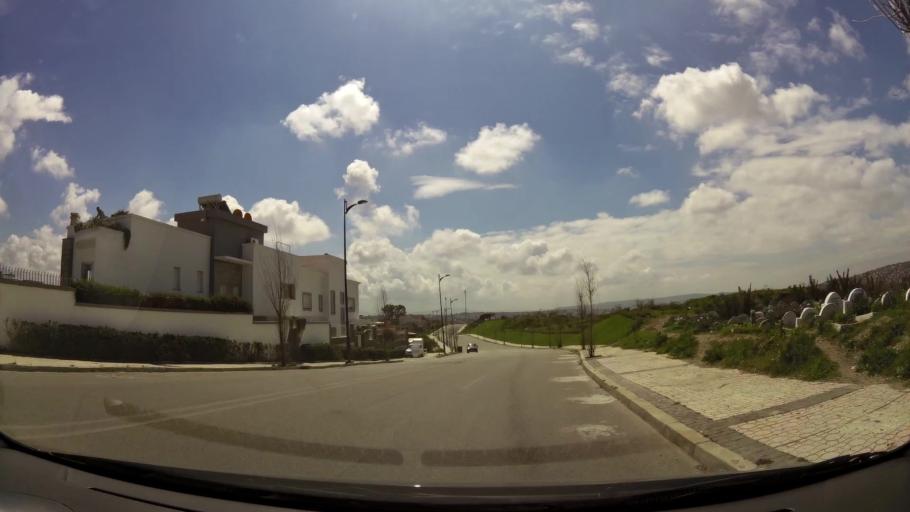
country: MA
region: Tanger-Tetouan
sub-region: Tanger-Assilah
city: Tangier
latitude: 35.7721
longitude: -5.8404
